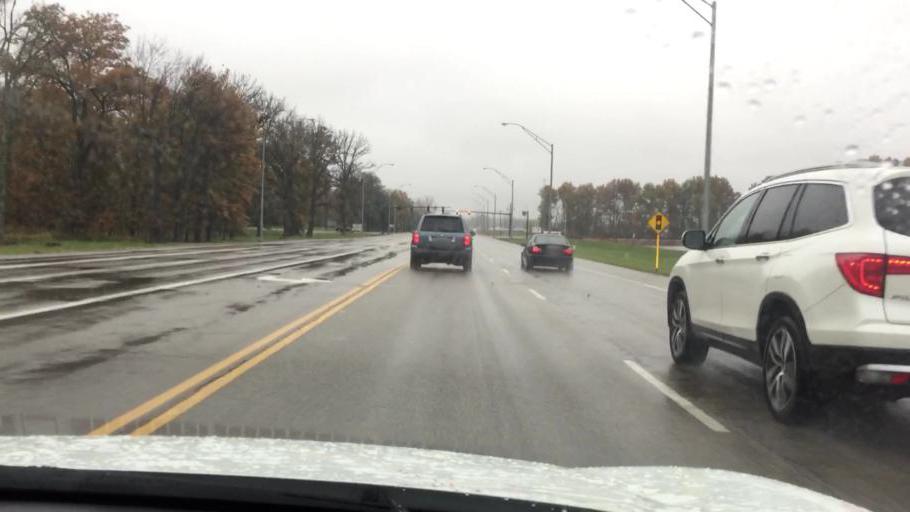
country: US
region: Ohio
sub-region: Champaign County
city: North Lewisburg
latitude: 40.2735
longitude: -83.5044
